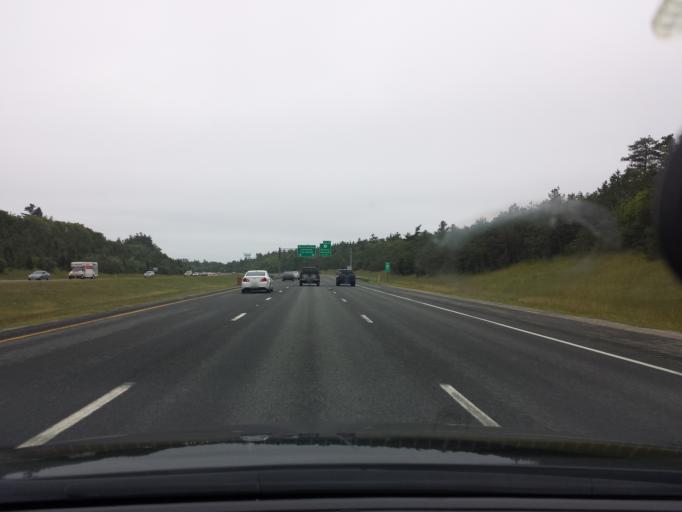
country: US
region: Massachusetts
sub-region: Barnstable County
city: Bourne
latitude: 41.7657
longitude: -70.5900
